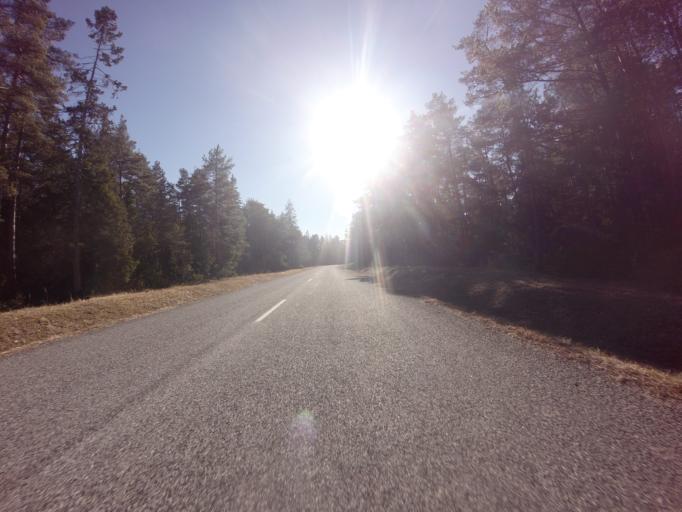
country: EE
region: Saare
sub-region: Kuressaare linn
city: Kuressaare
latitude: 58.5148
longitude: 22.3211
